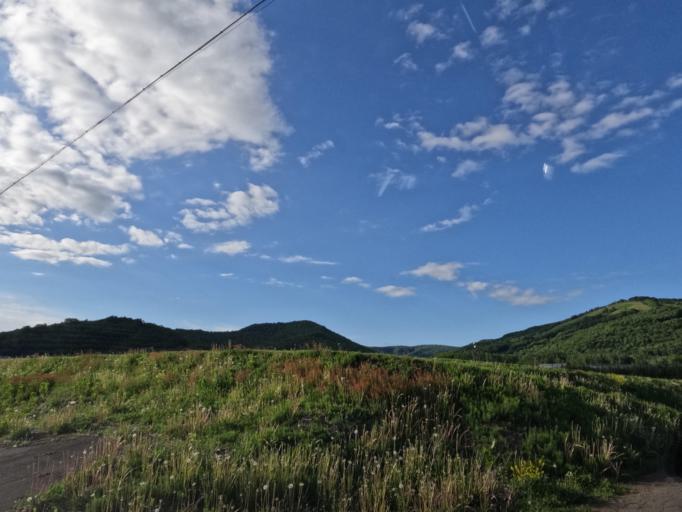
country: JP
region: Hokkaido
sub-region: Asahikawa-shi
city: Asahikawa
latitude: 43.9190
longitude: 142.4928
